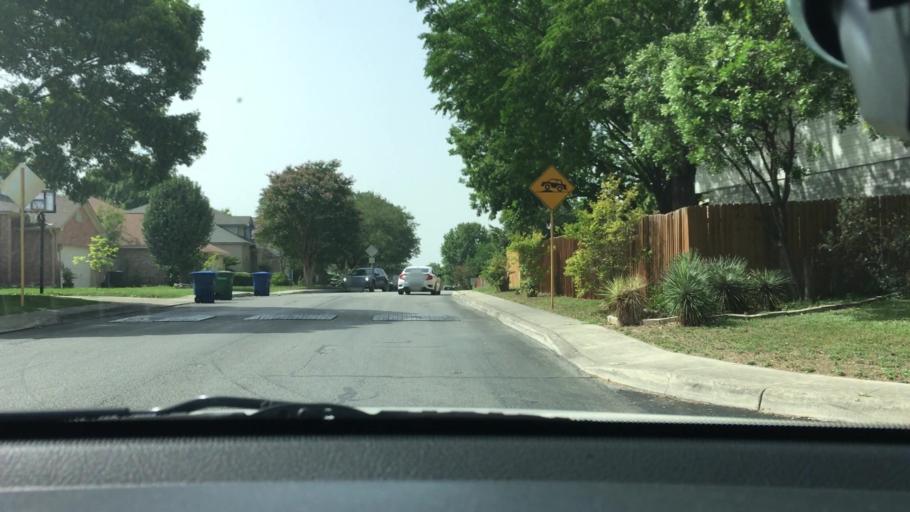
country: US
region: Texas
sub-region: Bexar County
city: Live Oak
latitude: 29.5780
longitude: -98.3832
